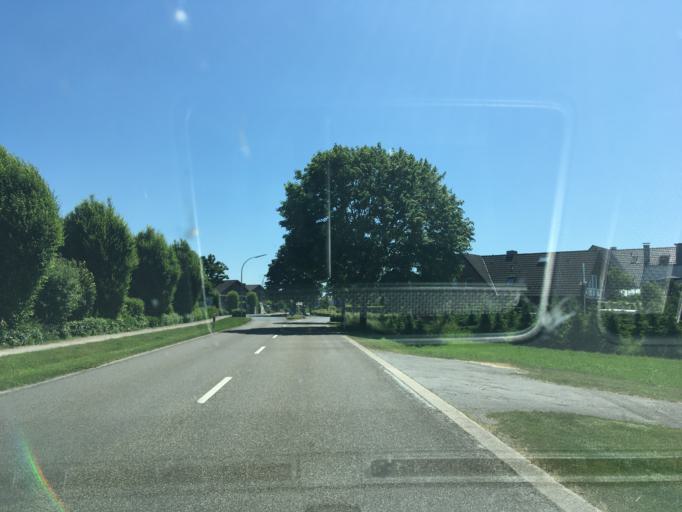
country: DE
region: North Rhine-Westphalia
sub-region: Regierungsbezirk Munster
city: Raesfeld
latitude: 51.7746
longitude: 6.8312
